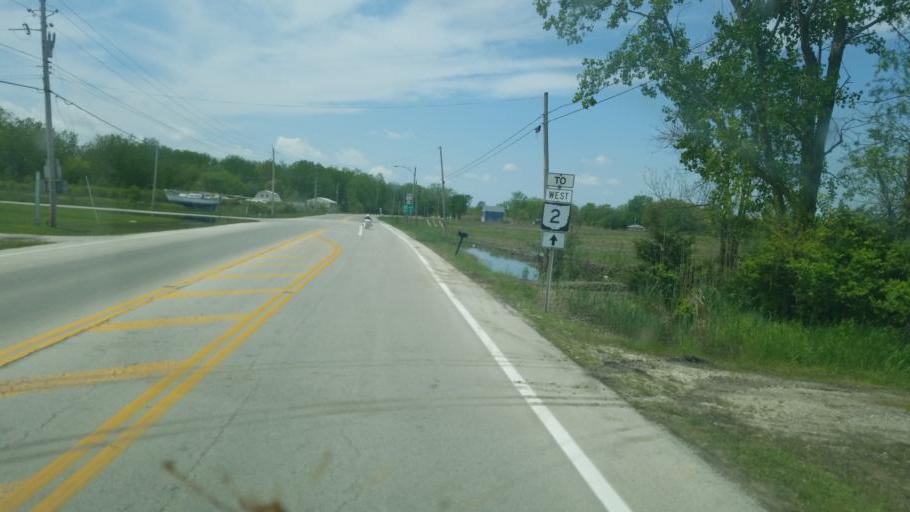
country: US
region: Ohio
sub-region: Ottawa County
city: Port Clinton
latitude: 41.5209
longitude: -82.9915
